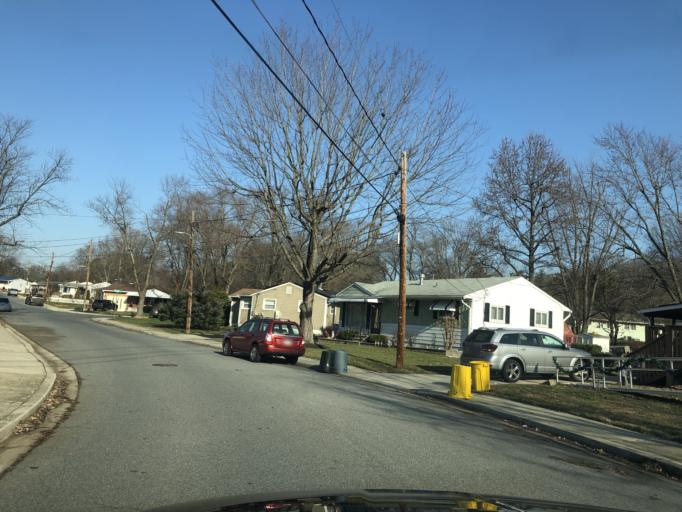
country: US
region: Maryland
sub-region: Anne Arundel County
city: Odenton
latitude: 39.0737
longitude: -76.6997
